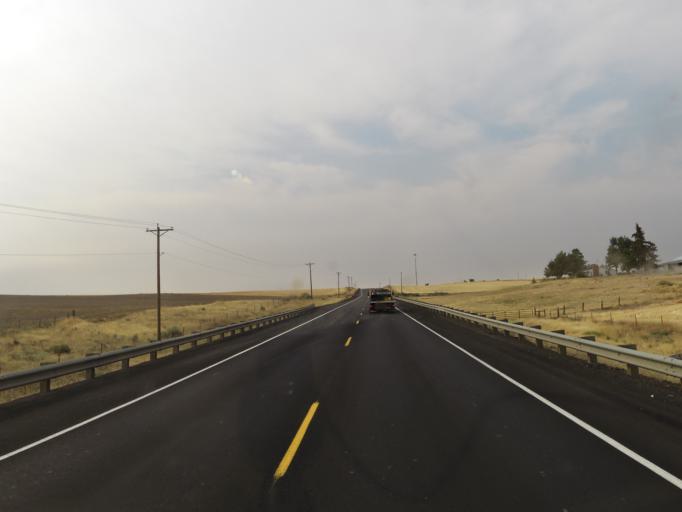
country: US
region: Oregon
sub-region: Sherman County
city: Moro
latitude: 45.3870
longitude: -120.7893
